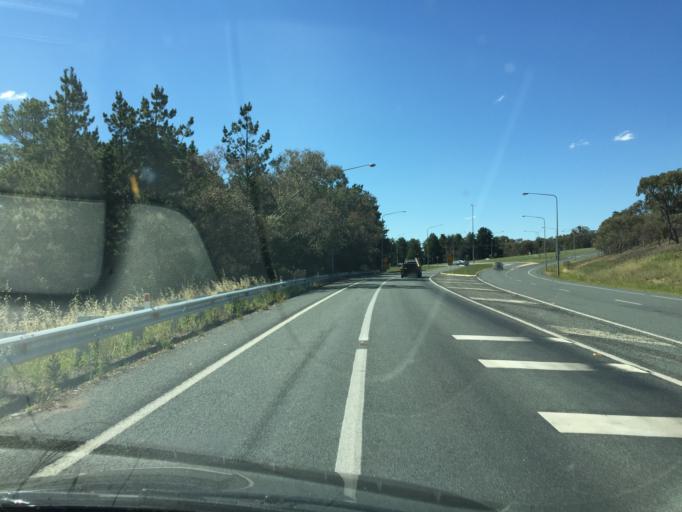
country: AU
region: Australian Capital Territory
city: Macarthur
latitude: -35.4381
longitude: 149.1262
